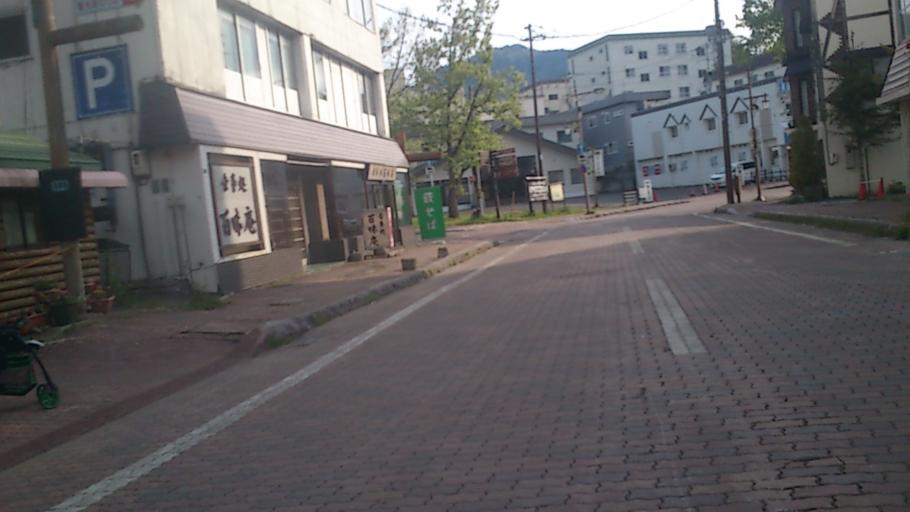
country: JP
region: Hokkaido
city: Bihoro
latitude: 43.4333
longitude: 144.0988
